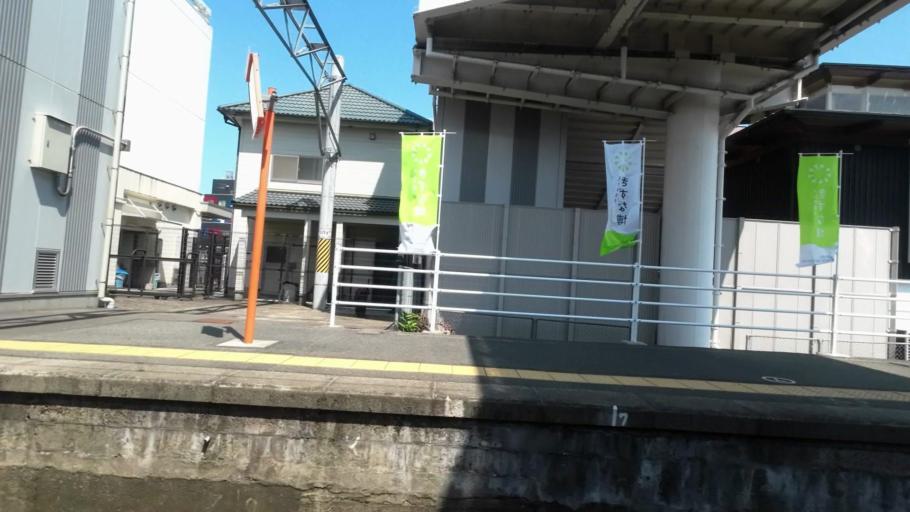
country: JP
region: Ehime
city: Saijo
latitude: 33.9125
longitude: 133.1879
